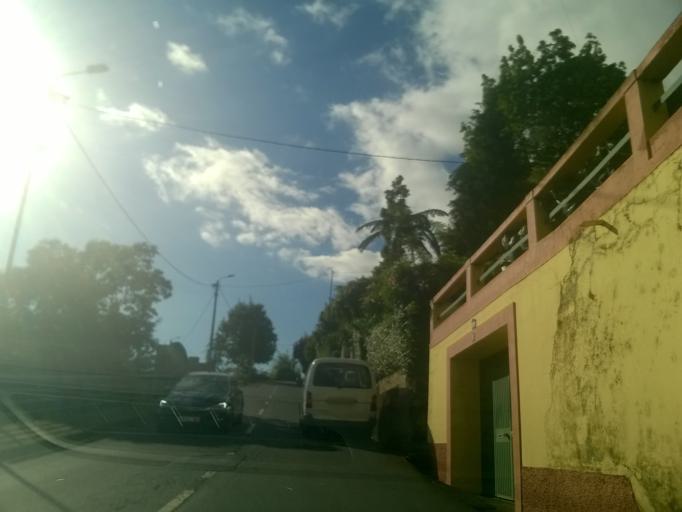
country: PT
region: Madeira
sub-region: Funchal
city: Nossa Senhora do Monte
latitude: 32.6763
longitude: -16.9055
